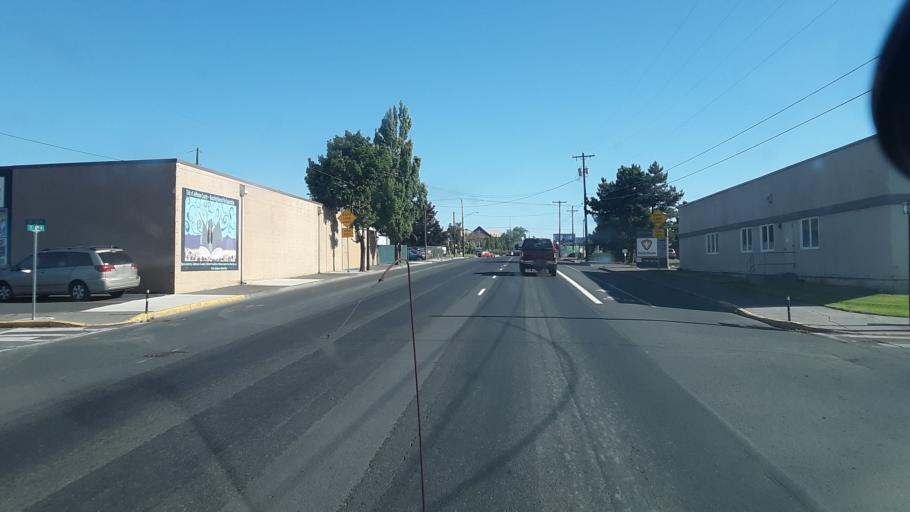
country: US
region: Oregon
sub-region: Jefferson County
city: Madras
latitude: 44.6265
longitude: -121.1306
